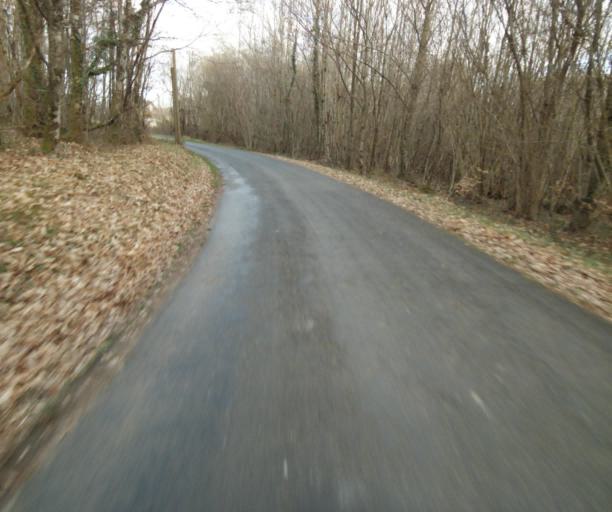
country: FR
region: Limousin
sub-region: Departement de la Correze
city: Uzerche
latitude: 45.3639
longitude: 1.5942
